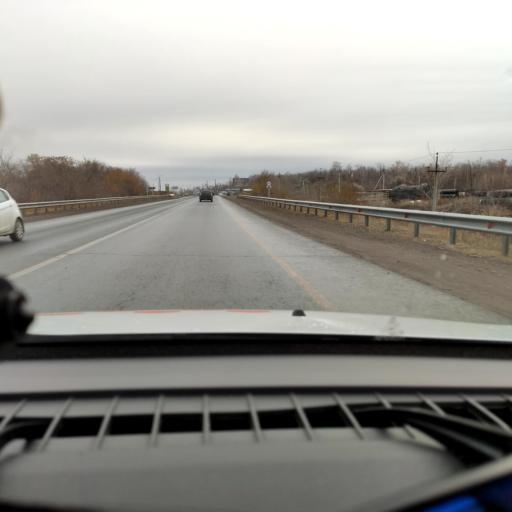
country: RU
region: Samara
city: Novokuybyshevsk
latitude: 53.0841
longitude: 50.0688
